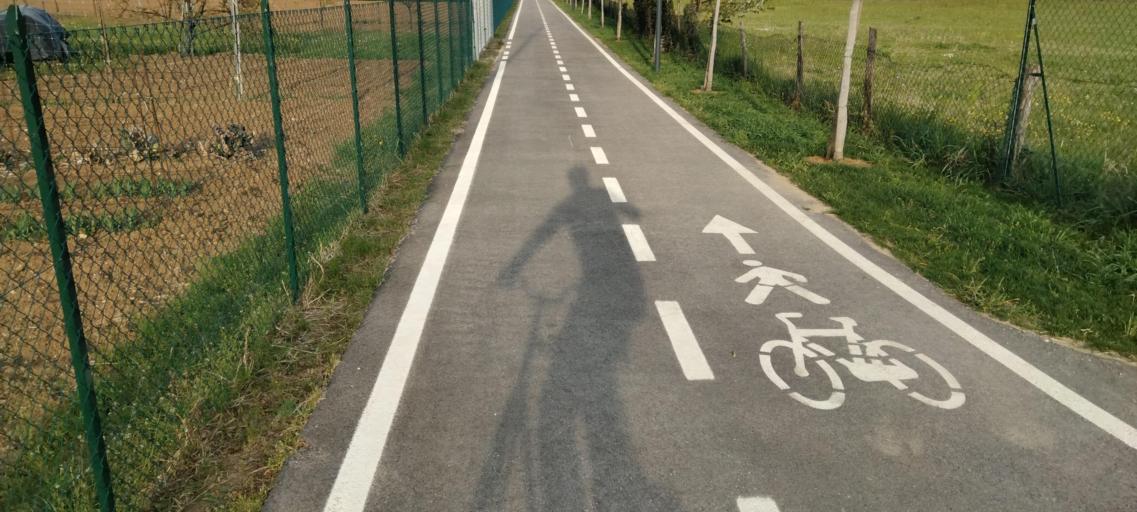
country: IT
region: Veneto
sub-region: Provincia di Vicenza
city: Costabissara
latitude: 45.5957
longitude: 11.4769
